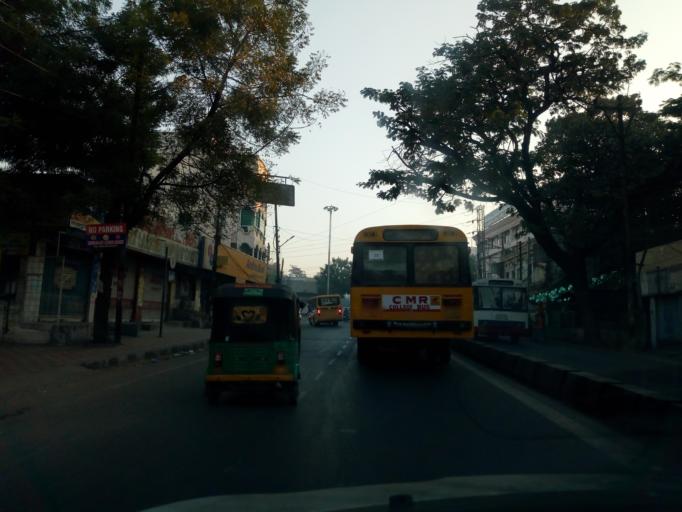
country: IN
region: Telangana
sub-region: Rangareddi
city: Gaddi Annaram
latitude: 17.4010
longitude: 78.5083
